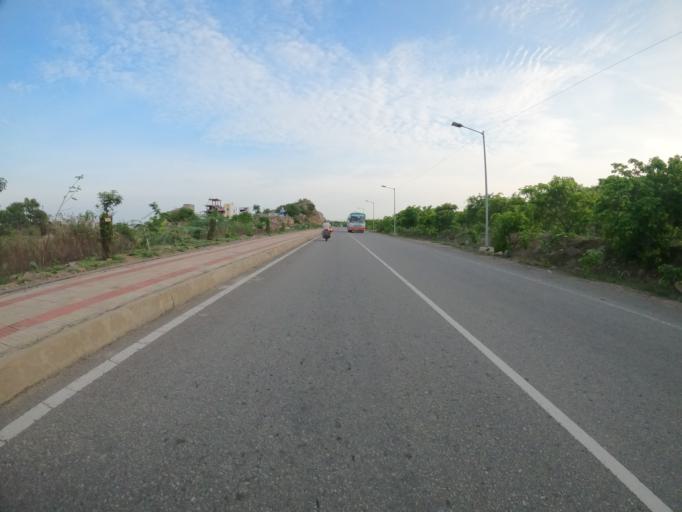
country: IN
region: Telangana
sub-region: Hyderabad
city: Hyderabad
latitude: 17.3785
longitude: 78.3501
